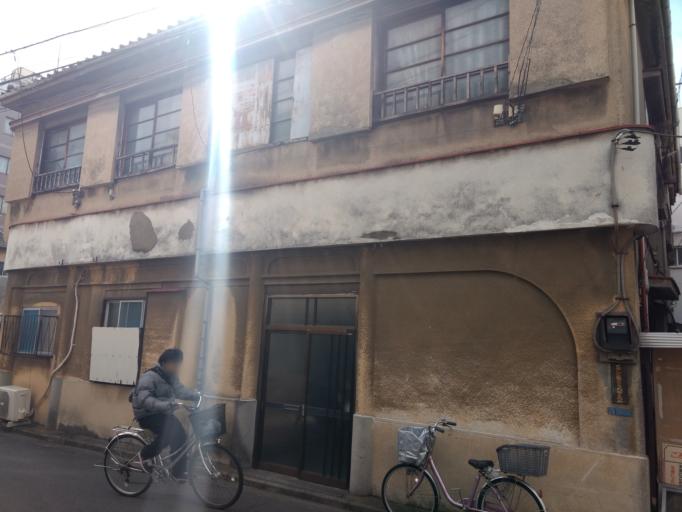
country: JP
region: Saitama
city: Soka
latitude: 35.7239
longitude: 139.7963
